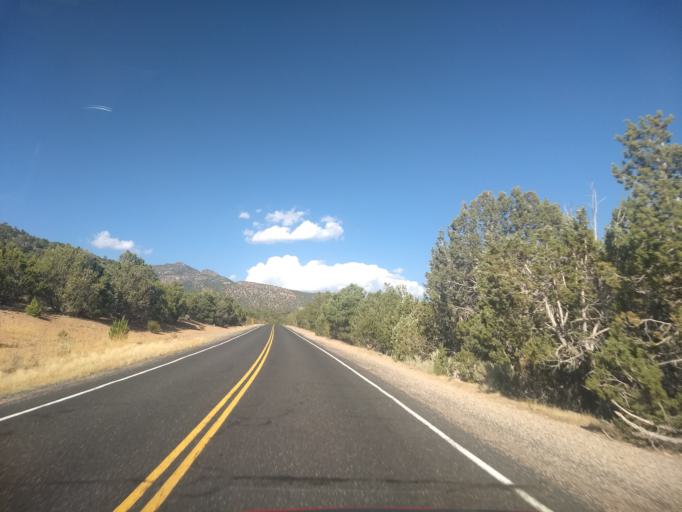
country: US
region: Utah
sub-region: Washington County
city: Enterprise
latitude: 37.4169
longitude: -113.5991
